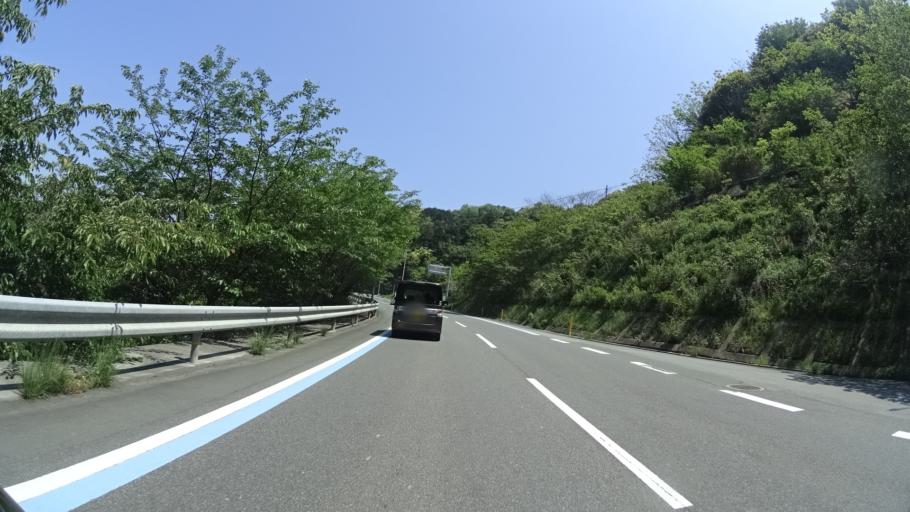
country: JP
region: Ehime
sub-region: Nishiuwa-gun
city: Ikata-cho
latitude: 33.5295
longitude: 132.3945
